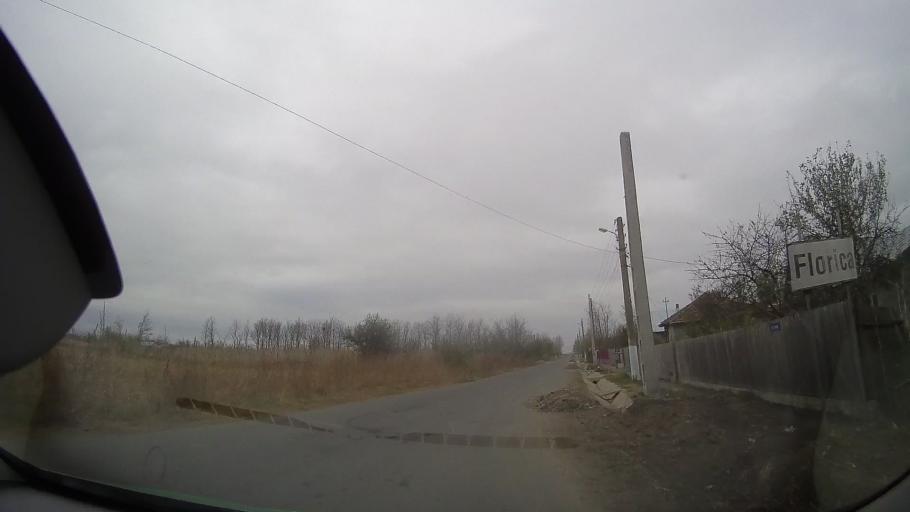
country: RO
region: Braila
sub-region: Comuna Rosiori
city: Rosiori
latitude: 44.8342
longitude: 27.3367
